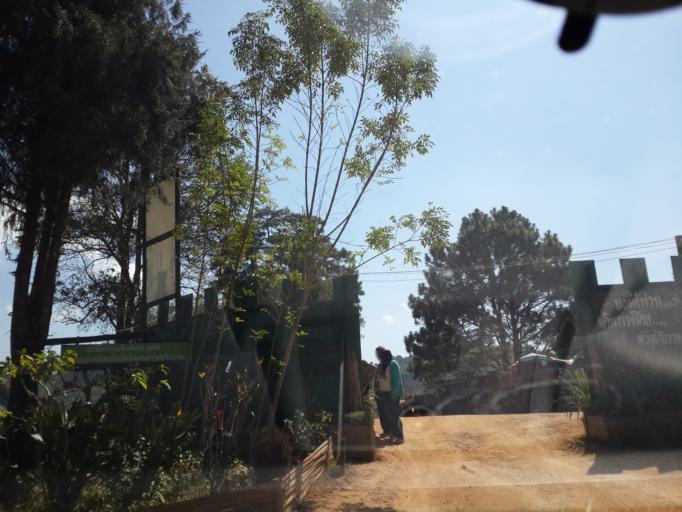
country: TH
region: Chiang Mai
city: Fang
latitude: 19.9400
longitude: 99.0415
